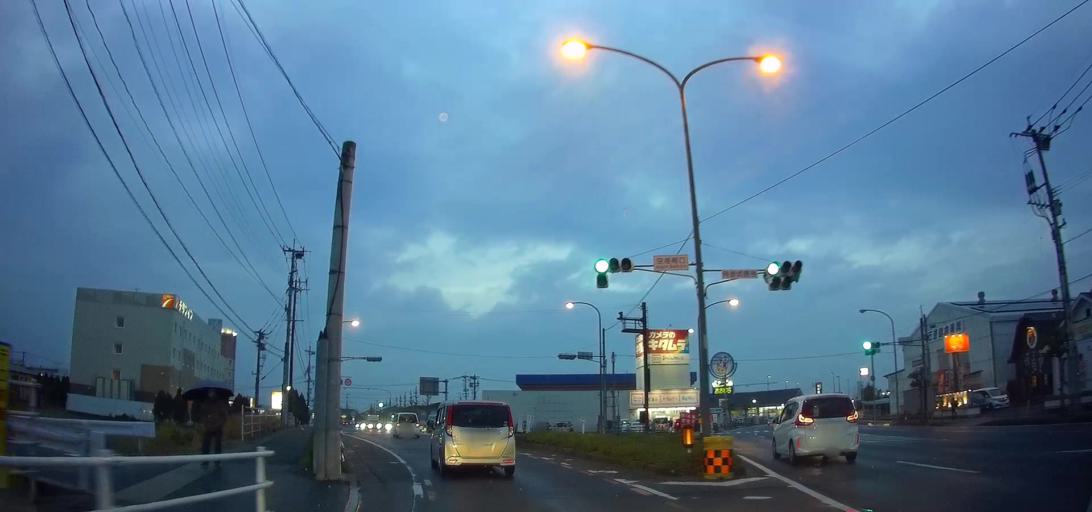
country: JP
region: Nagasaki
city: Omura
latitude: 32.9117
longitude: 129.9514
